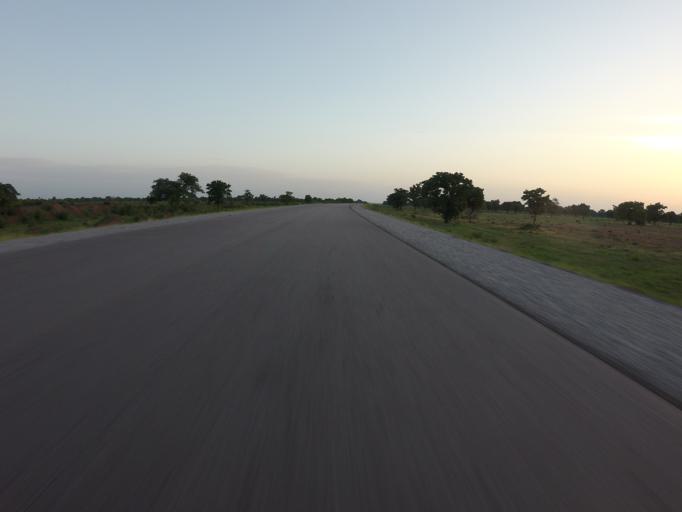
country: GH
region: Northern
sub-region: Yendi
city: Yendi
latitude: 9.9488
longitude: -0.1575
